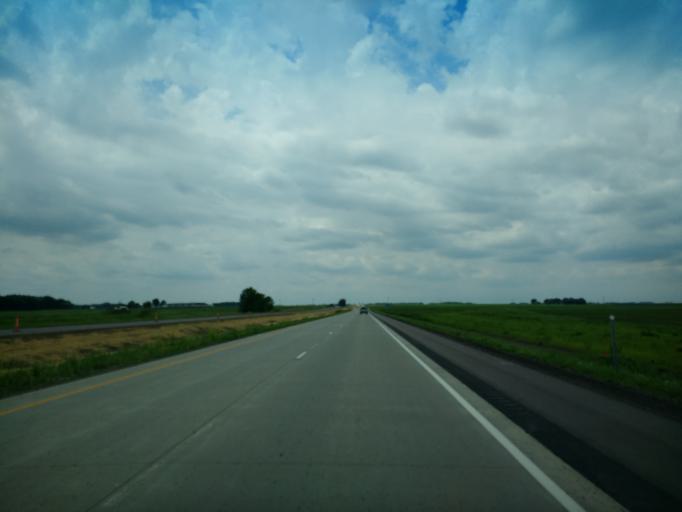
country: US
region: Minnesota
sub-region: Cottonwood County
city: Mountain Lake
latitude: 43.9260
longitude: -94.9728
